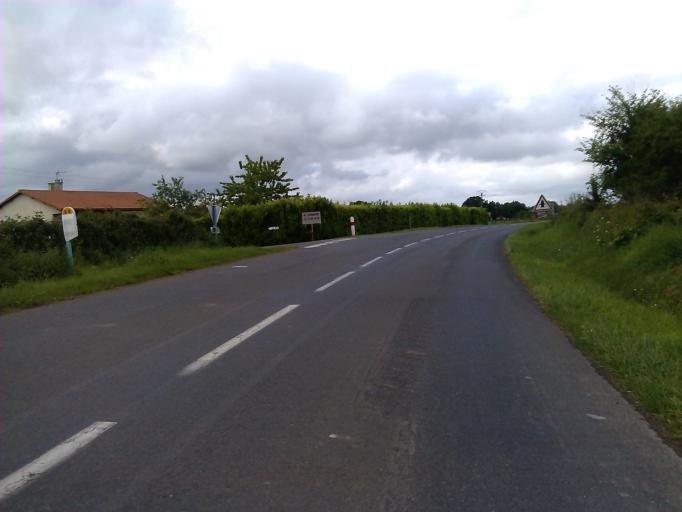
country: FR
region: Poitou-Charentes
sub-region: Departement de la Vienne
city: Availles-Limouzine
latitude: 46.1977
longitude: 0.6438
